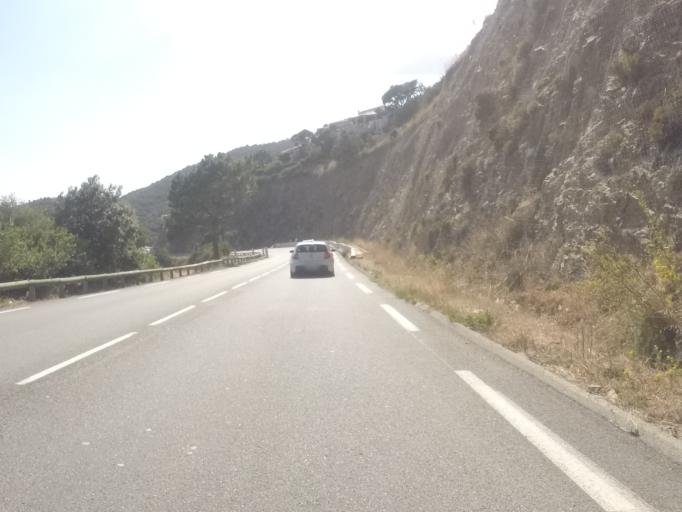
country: FR
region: Corsica
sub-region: Departement de la Corse-du-Sud
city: Sari-Solenzara
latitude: 41.7210
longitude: 9.4042
